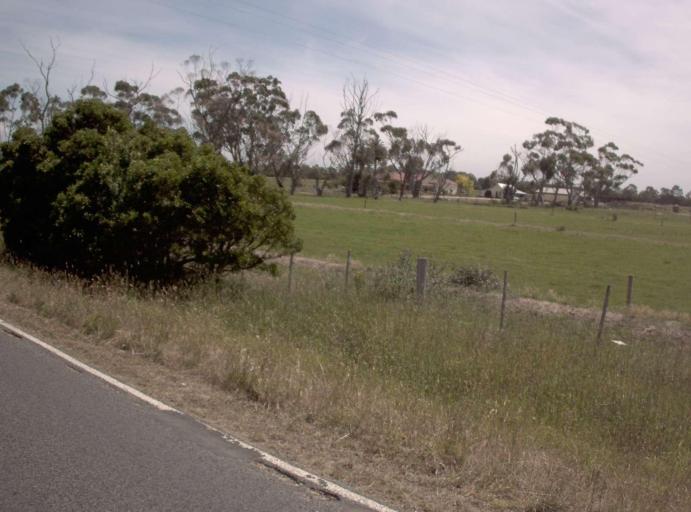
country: AU
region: Victoria
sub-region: Wellington
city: Heyfield
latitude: -38.0662
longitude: 146.8716
